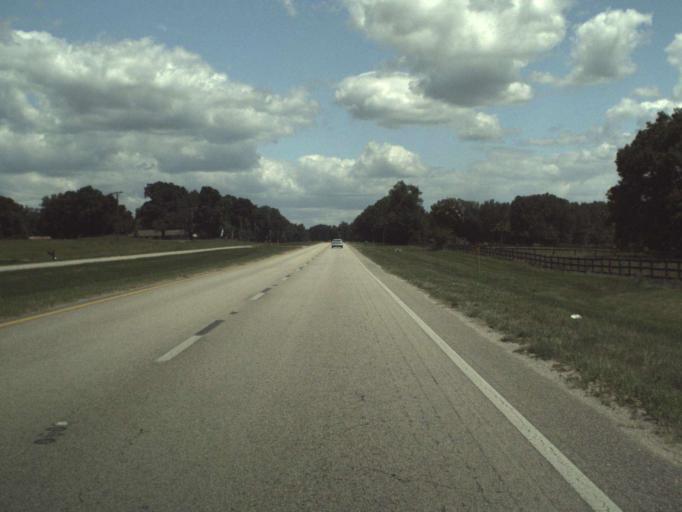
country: US
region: Florida
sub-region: Marion County
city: Citra
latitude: 29.3557
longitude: -82.1630
